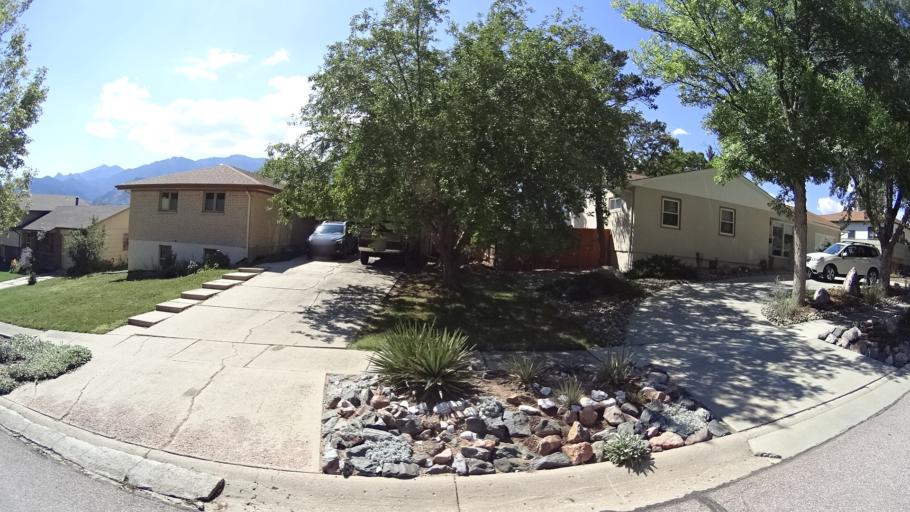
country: US
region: Colorado
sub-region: El Paso County
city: Colorado Springs
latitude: 38.8616
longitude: -104.8621
